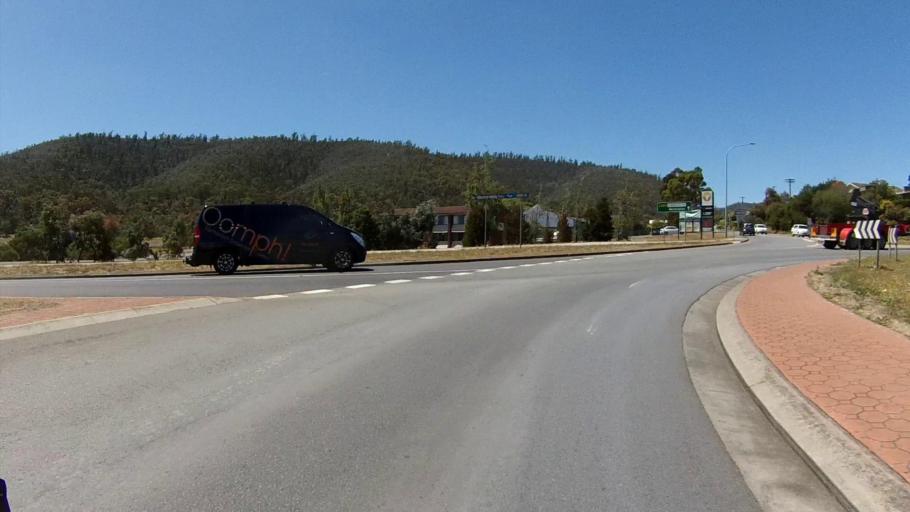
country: AU
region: Tasmania
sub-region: Clarence
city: Warrane
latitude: -42.8561
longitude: 147.3942
